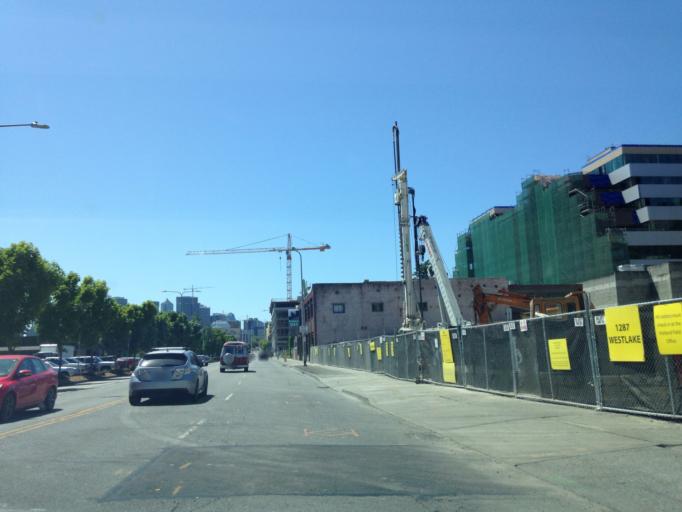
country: US
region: Washington
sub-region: King County
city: Seattle
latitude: 47.6322
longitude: -122.3410
